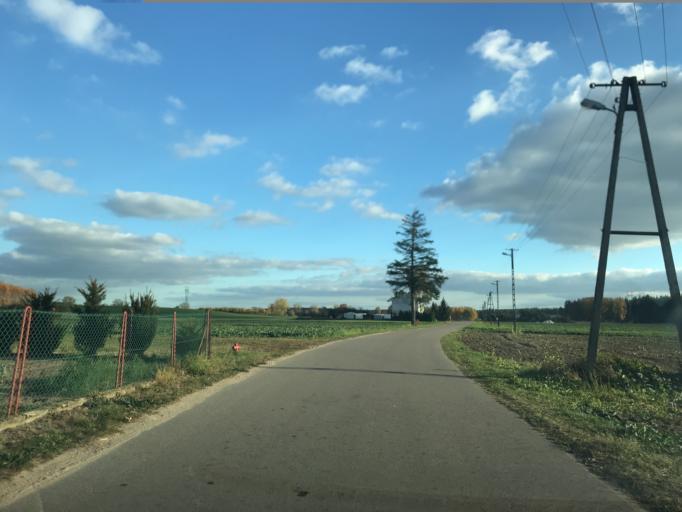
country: PL
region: Warmian-Masurian Voivodeship
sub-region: Powiat dzialdowski
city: Rybno
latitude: 53.3803
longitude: 19.8201
